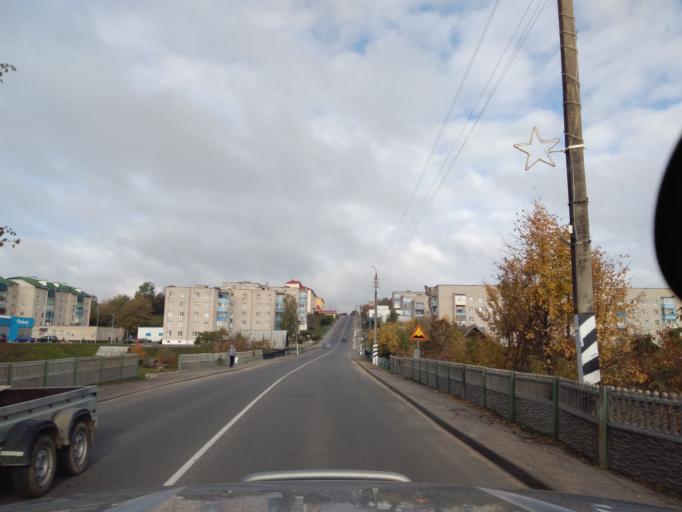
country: BY
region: Minsk
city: Kapyl'
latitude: 53.1482
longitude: 27.0948
